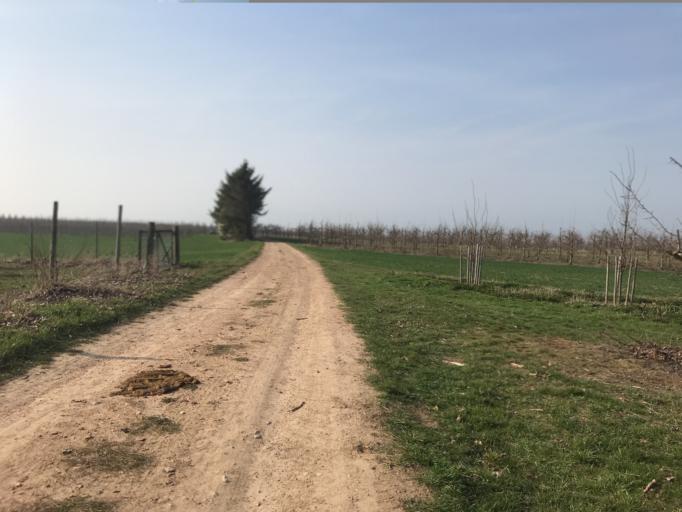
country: DE
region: Rheinland-Pfalz
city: Wackernheim
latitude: 49.9843
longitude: 8.1362
